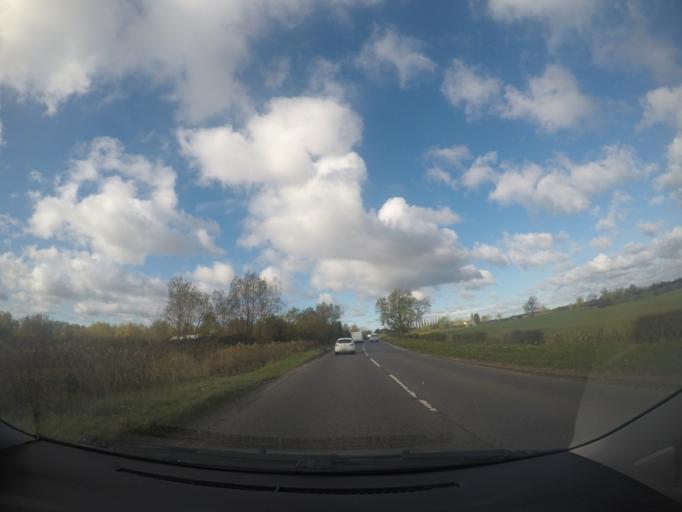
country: GB
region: England
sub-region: City of York
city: Nether Poppleton
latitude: 53.9756
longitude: -1.1771
